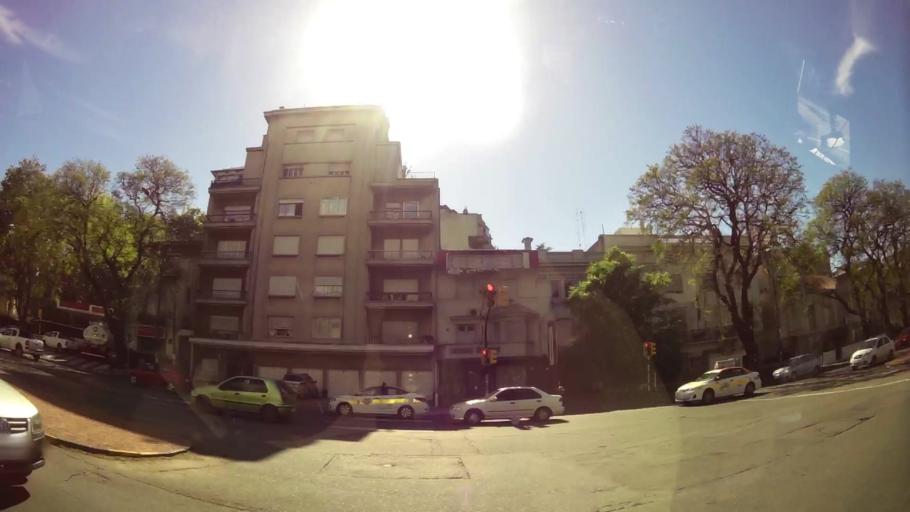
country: UY
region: Montevideo
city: Montevideo
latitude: -34.9027
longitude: -56.1641
